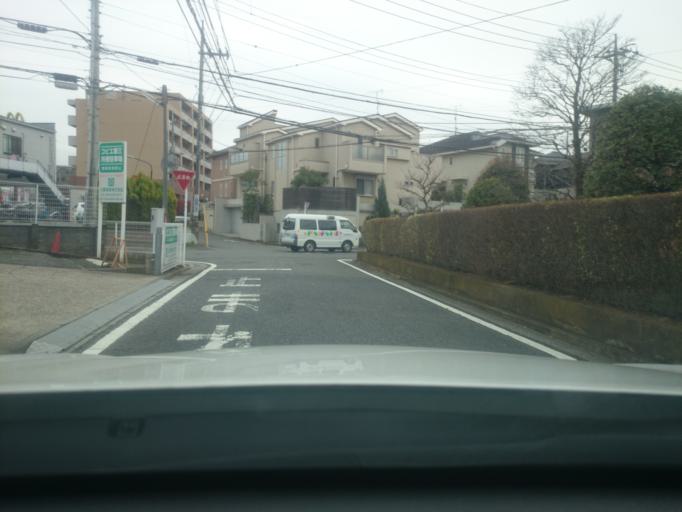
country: JP
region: Tokyo
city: Chofugaoka
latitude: 35.5648
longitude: 139.5765
